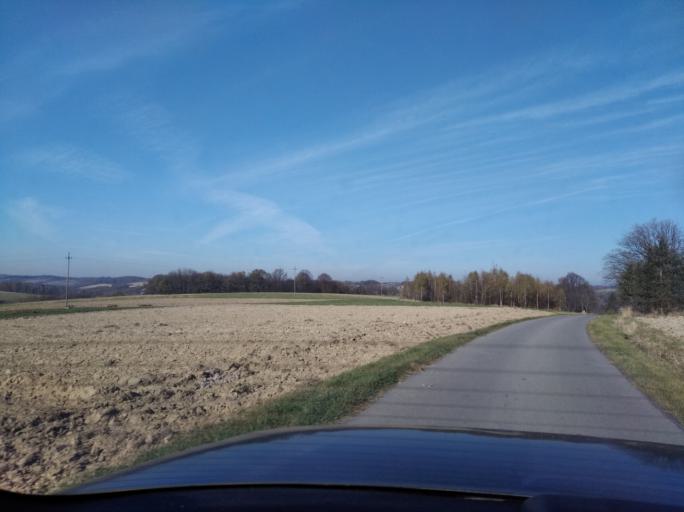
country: PL
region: Subcarpathian Voivodeship
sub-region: Powiat ropczycko-sedziszowski
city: Wielopole Skrzynskie
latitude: 49.9223
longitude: 21.5586
